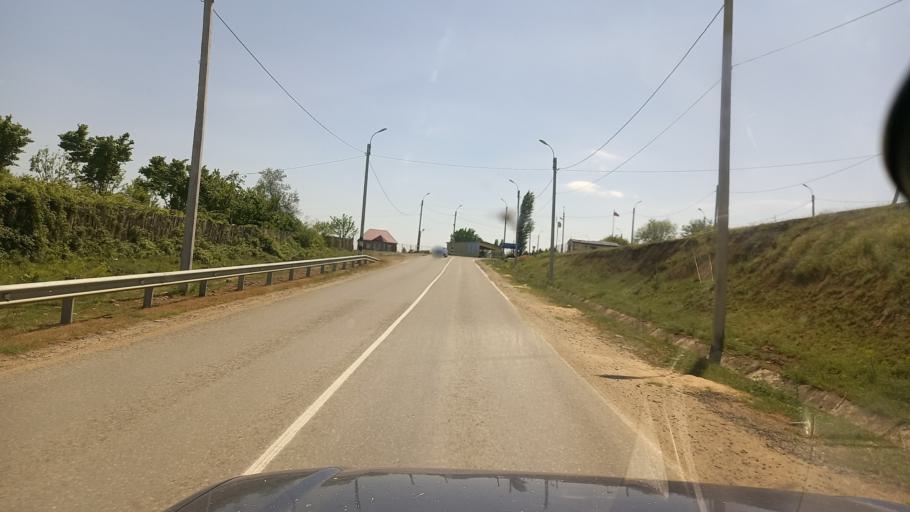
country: RU
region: Dagestan
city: Novaya Maka
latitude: 41.7373
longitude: 48.4424
